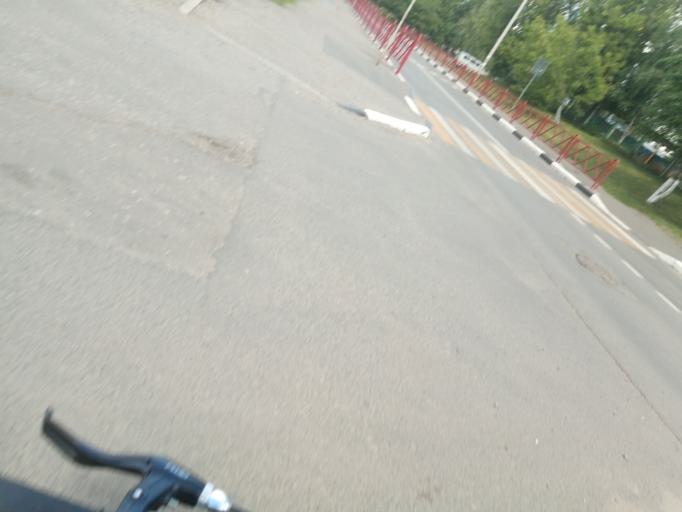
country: RU
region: Jaroslavl
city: Yaroslavl
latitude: 57.6573
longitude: 39.9565
